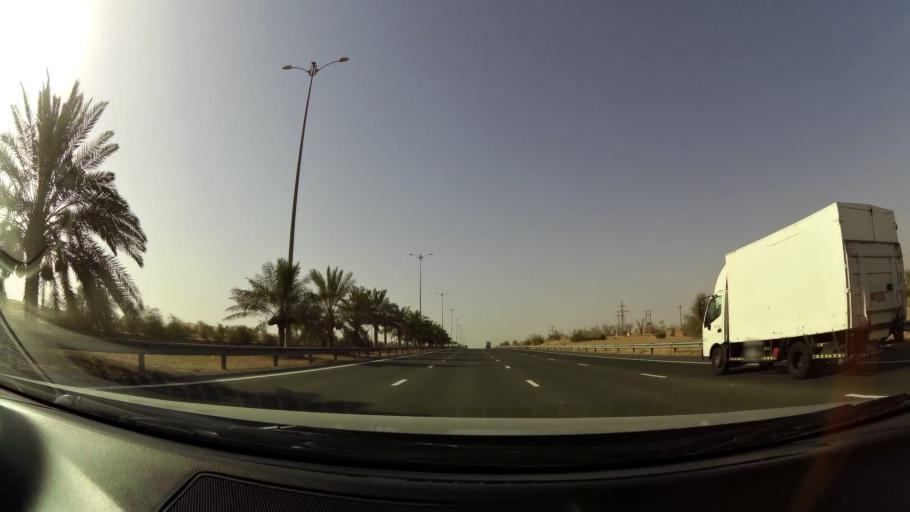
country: OM
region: Al Buraimi
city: Al Buraymi
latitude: 24.6217
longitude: 55.7249
